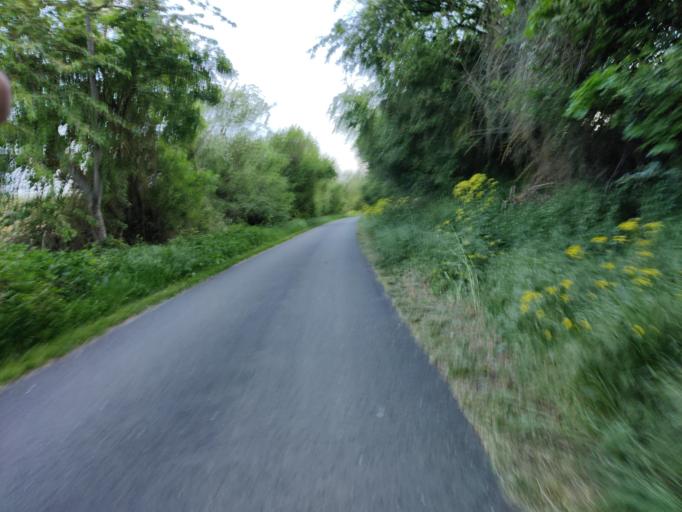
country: DE
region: Saxony-Anhalt
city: Karsdorf
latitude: 51.2511
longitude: 11.6563
